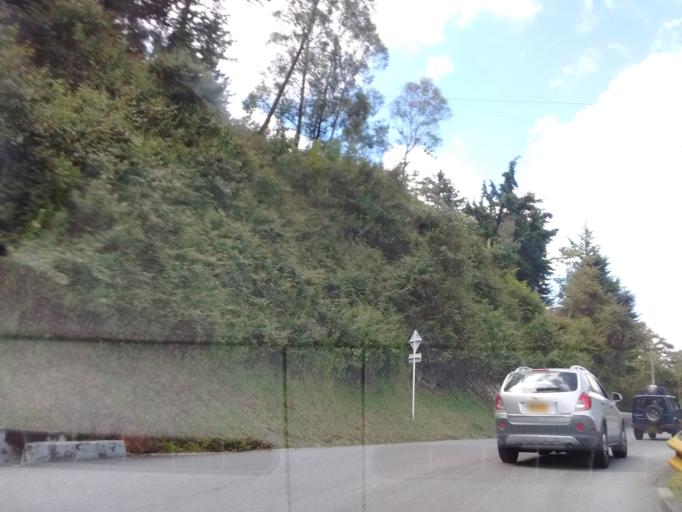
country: CO
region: Antioquia
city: Medellin
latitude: 6.2416
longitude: -75.5120
